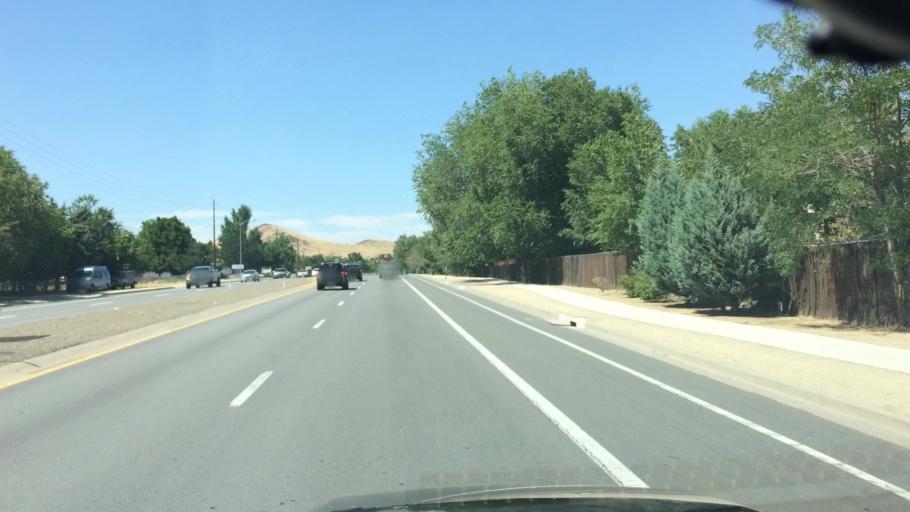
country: US
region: Nevada
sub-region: Washoe County
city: Sparks
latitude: 39.5489
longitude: -119.7337
